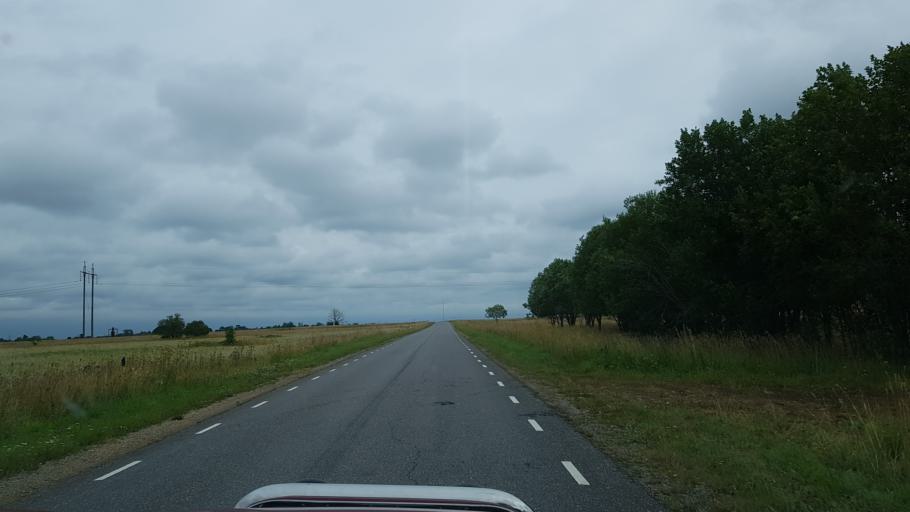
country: EE
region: Ida-Virumaa
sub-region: Puessi linn
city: Pussi
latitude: 59.3957
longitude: 27.0180
